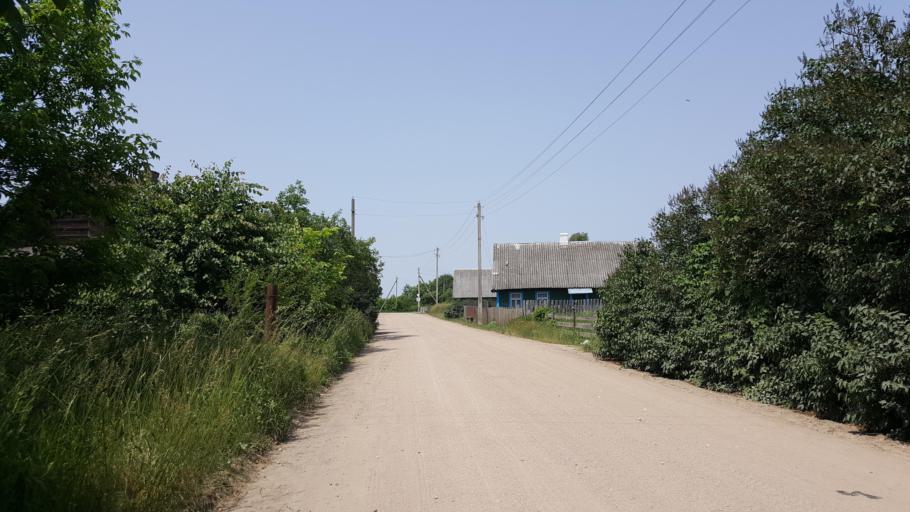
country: BY
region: Brest
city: Kamyanyets
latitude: 52.4802
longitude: 23.8783
